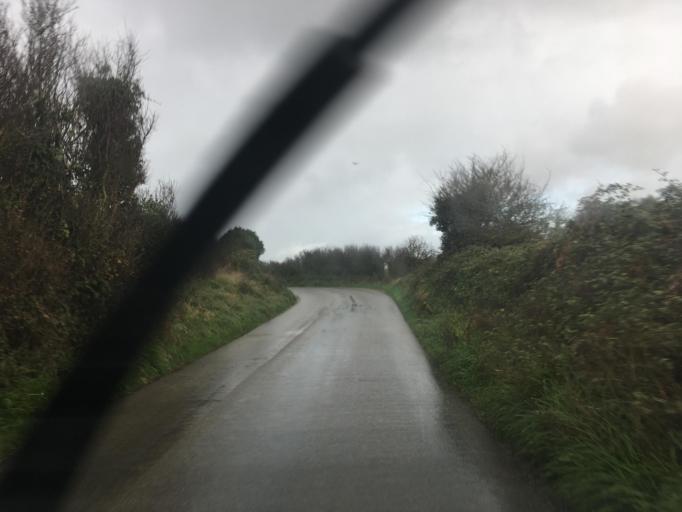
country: FR
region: Lower Normandy
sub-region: Departement de la Manche
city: Reville
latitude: 49.6894
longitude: -1.2793
